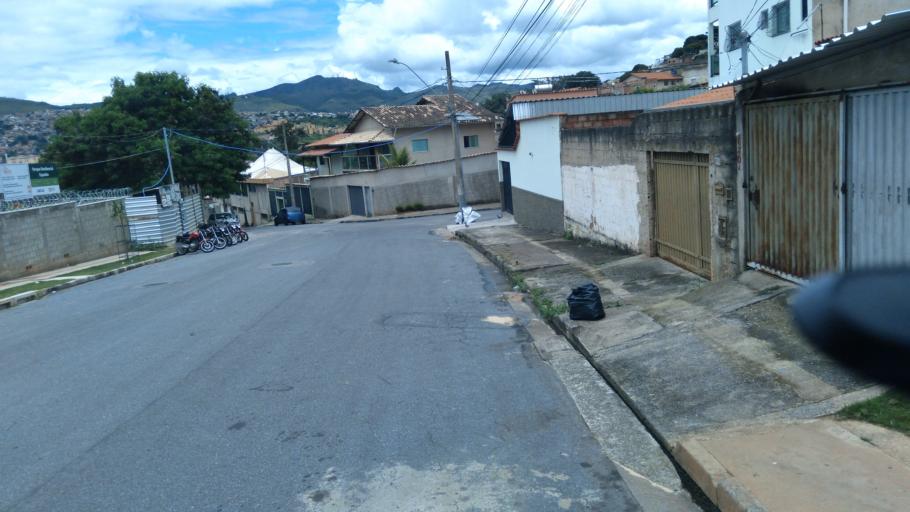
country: BR
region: Minas Gerais
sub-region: Belo Horizonte
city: Belo Horizonte
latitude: -19.8952
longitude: -43.8858
